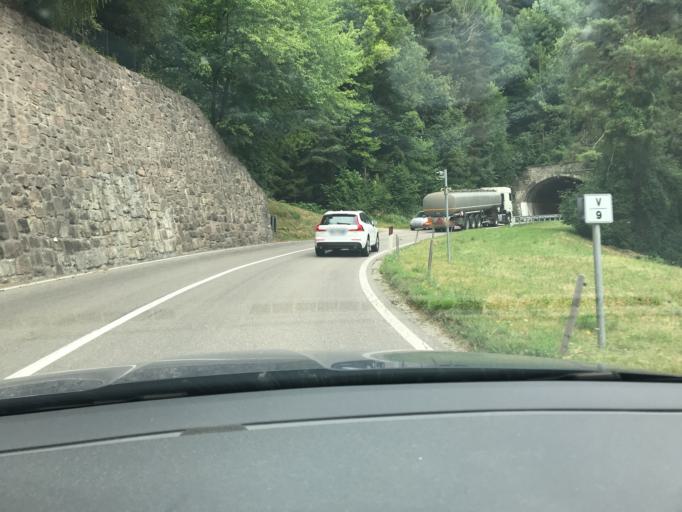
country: IT
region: Trentino-Alto Adige
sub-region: Bolzano
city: Laion
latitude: 46.5995
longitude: 11.5774
